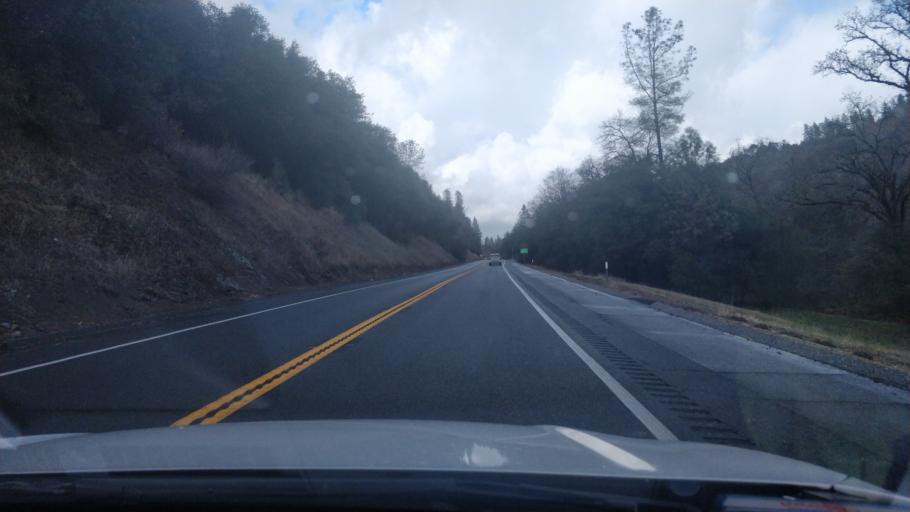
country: US
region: California
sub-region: Nevada County
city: Lake of the Pines
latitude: 39.0844
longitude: -121.0869
